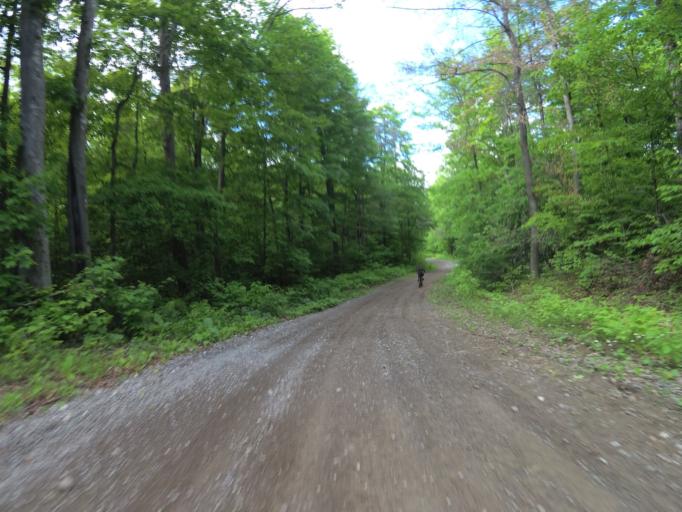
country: CA
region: Ontario
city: Renfrew
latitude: 45.1350
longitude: -76.8754
